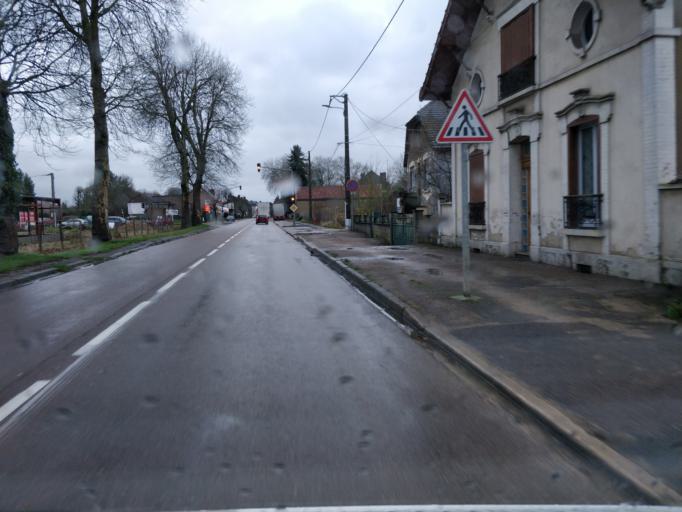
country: FR
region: Bourgogne
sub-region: Departement de l'Yonne
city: Thorigny-sur-Oreuse
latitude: 48.2368
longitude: 3.5513
